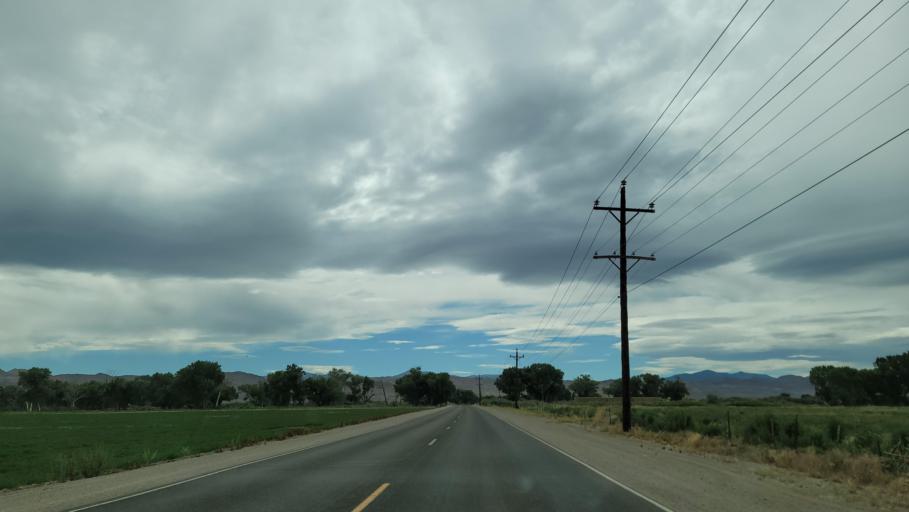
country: US
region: Nevada
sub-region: Lyon County
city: Yerington
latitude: 39.0482
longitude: -119.1587
